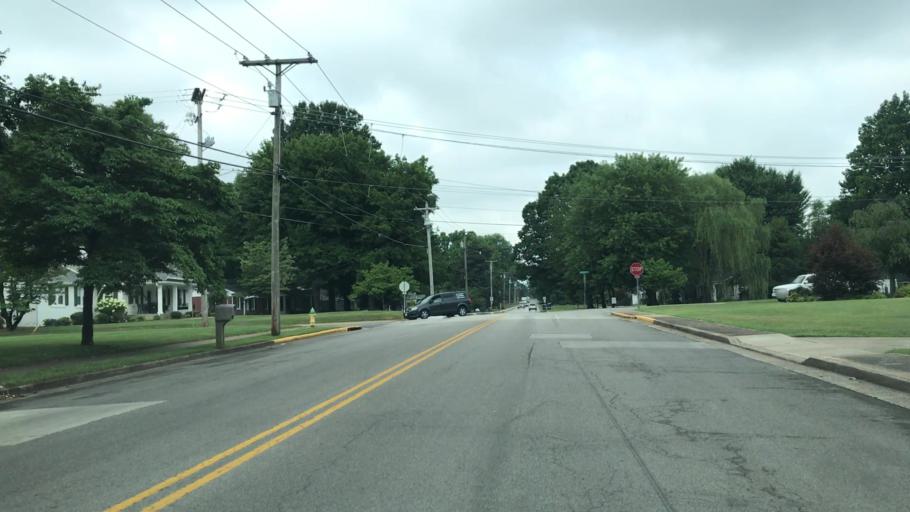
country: US
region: Kentucky
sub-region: Warren County
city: Bowling Green
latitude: 36.9827
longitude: -86.4268
